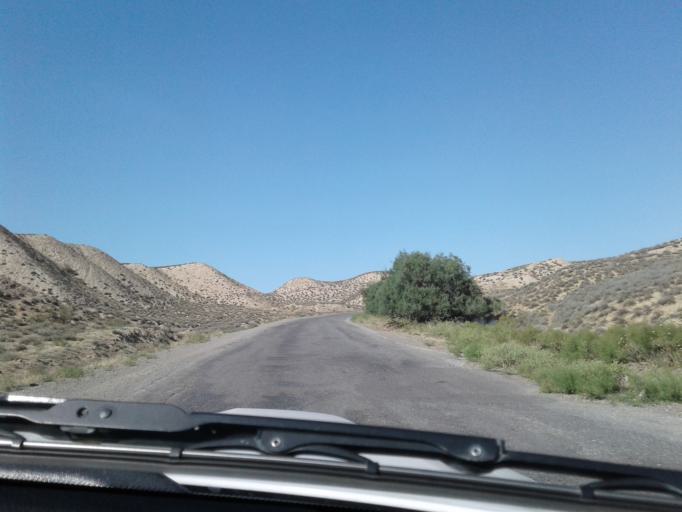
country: TM
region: Balkan
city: Magtymguly
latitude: 38.6538
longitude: 56.2777
